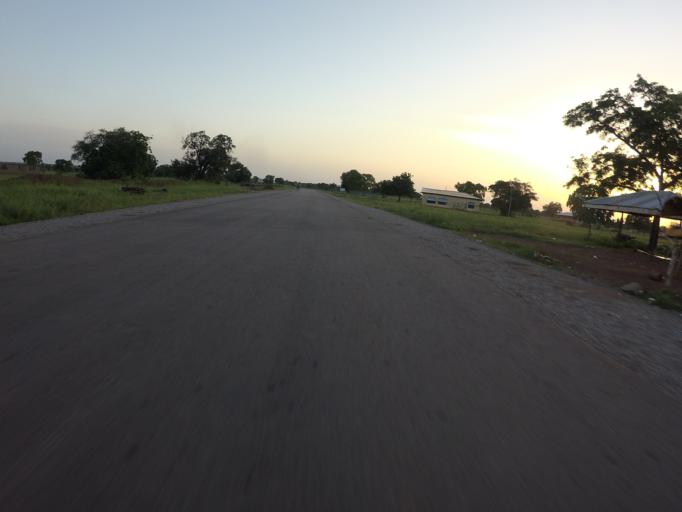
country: GH
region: Northern
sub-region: Yendi
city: Yendi
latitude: 9.9625
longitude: -0.1416
